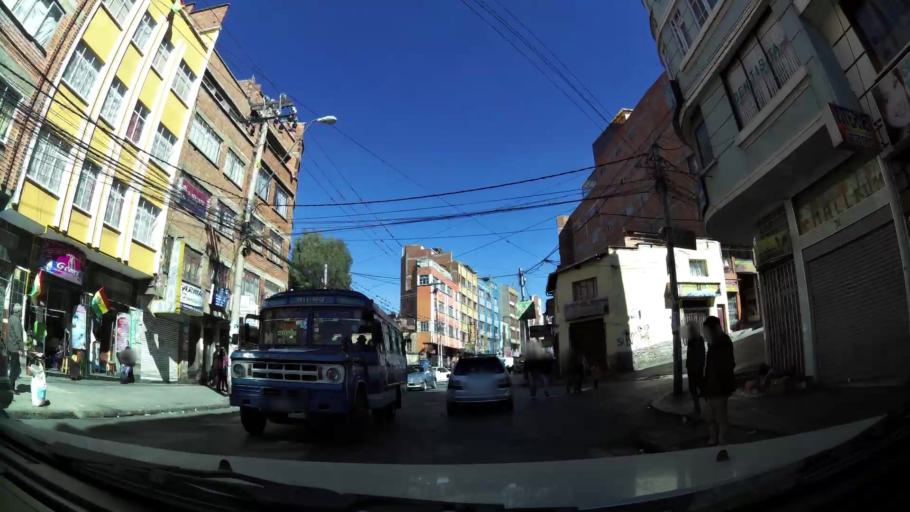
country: BO
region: La Paz
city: La Paz
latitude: -16.4983
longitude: -68.1444
